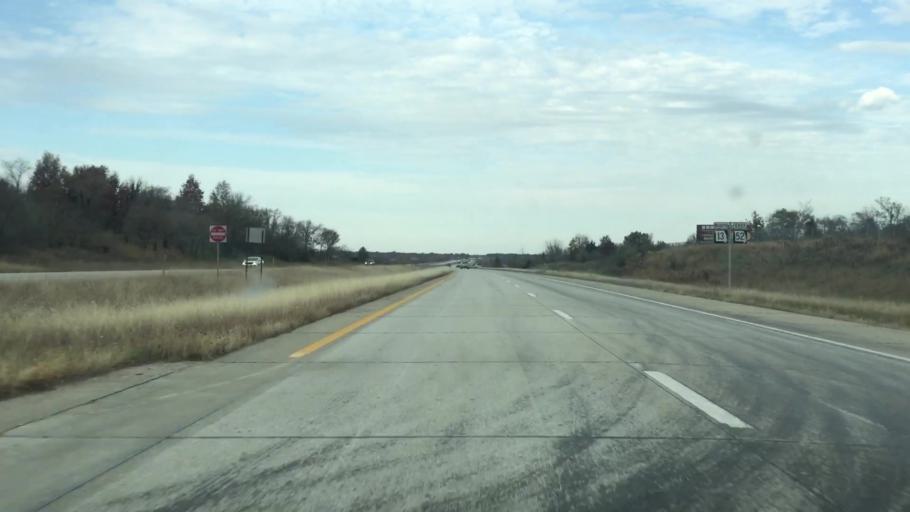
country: US
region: Missouri
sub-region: Henry County
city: Clinton
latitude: 38.3084
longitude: -93.7583
